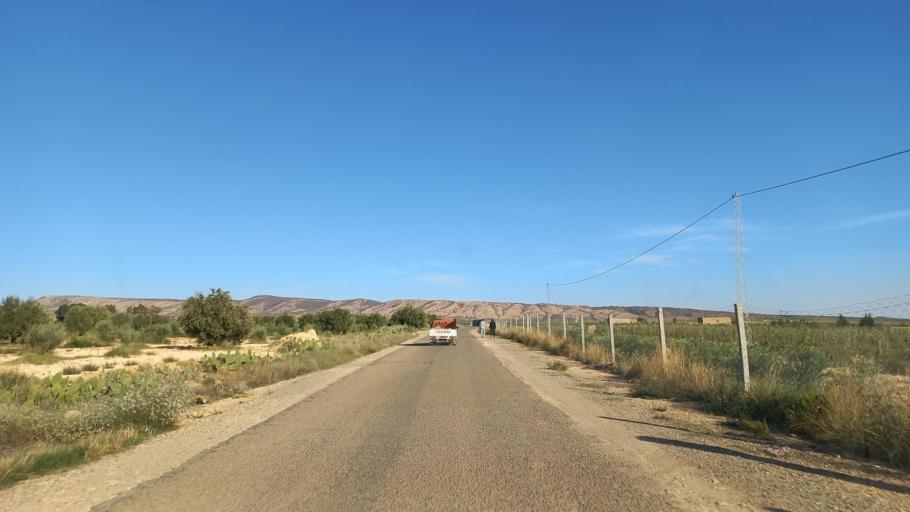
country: TN
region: Al Qasrayn
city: Sbiba
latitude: 35.3345
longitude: 9.0933
